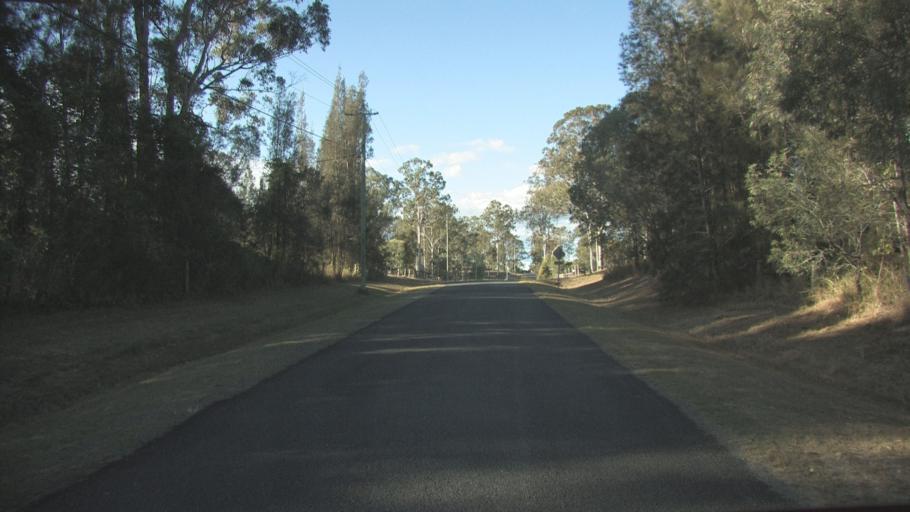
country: AU
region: Queensland
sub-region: Logan
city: Cedar Vale
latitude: -27.9297
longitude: 153.0667
